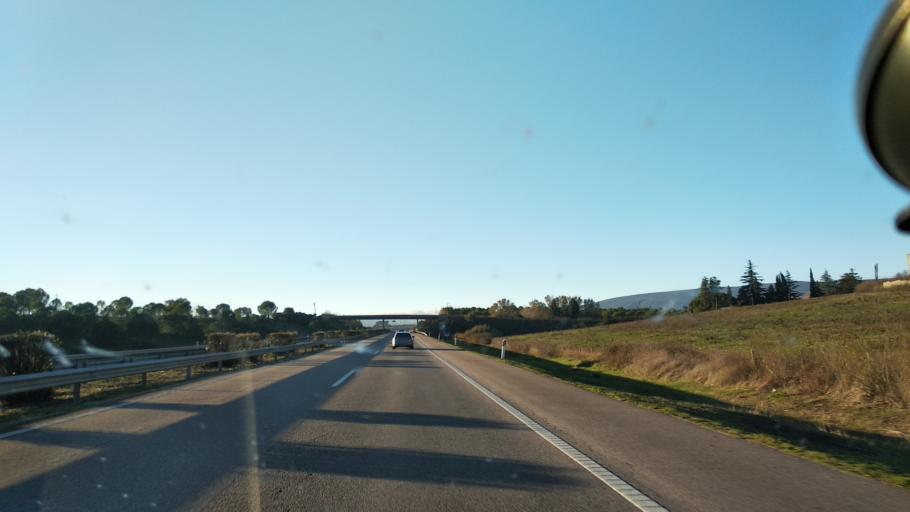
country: PT
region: Santarem
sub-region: Torres Novas
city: Torres Novas
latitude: 39.4669
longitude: -8.5605
